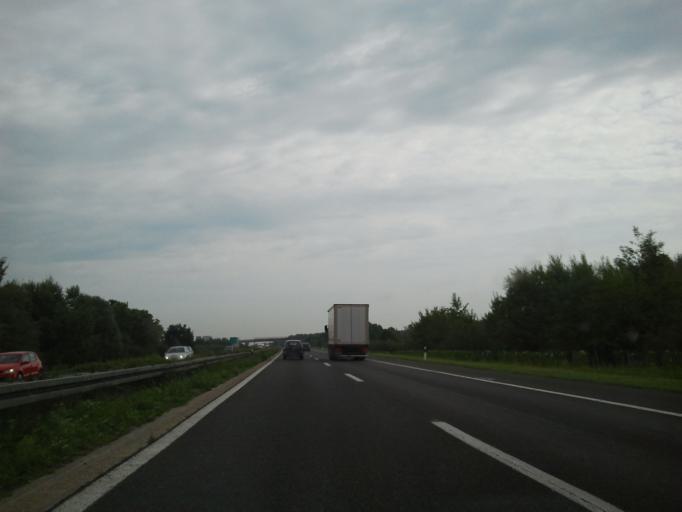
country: HR
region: Karlovacka
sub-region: Grad Karlovac
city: Karlovac
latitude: 45.5679
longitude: 15.6156
